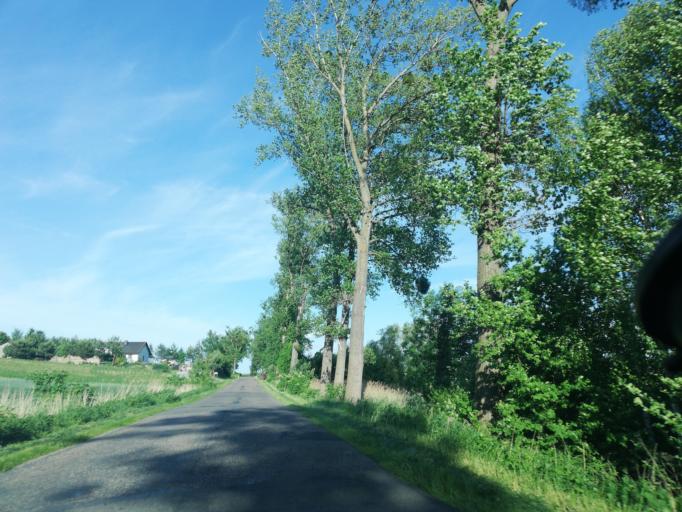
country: PL
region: Kujawsko-Pomorskie
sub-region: Powiat golubsko-dobrzynski
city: Zbojno
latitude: 53.0394
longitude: 19.0909
